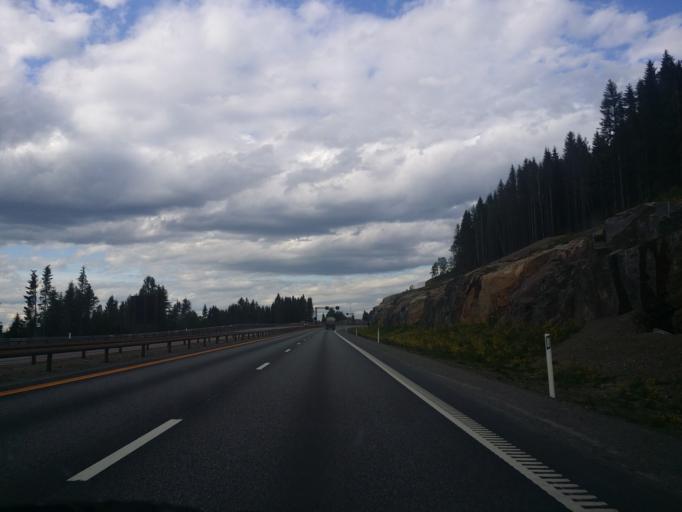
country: NO
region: Hedmark
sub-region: Stange
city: Stange
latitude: 60.5692
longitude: 11.2616
